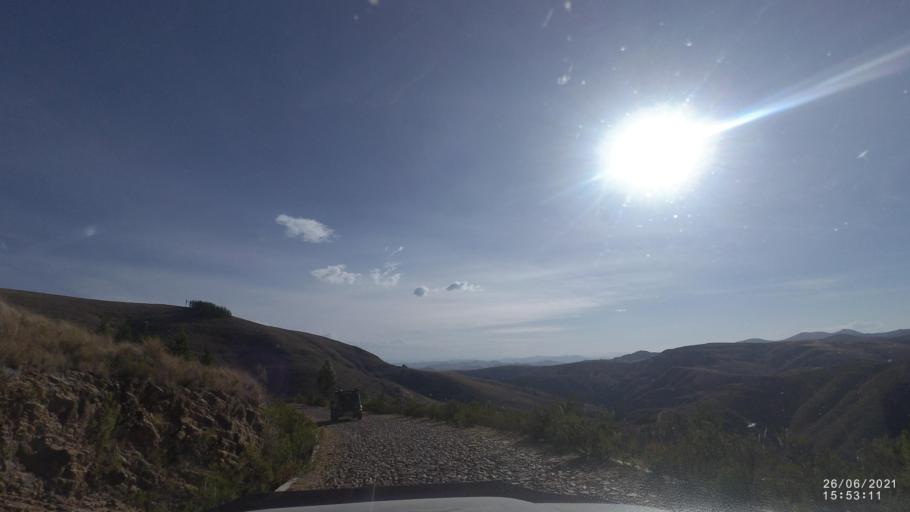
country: BO
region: Cochabamba
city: Arani
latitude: -17.8371
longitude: -65.7062
